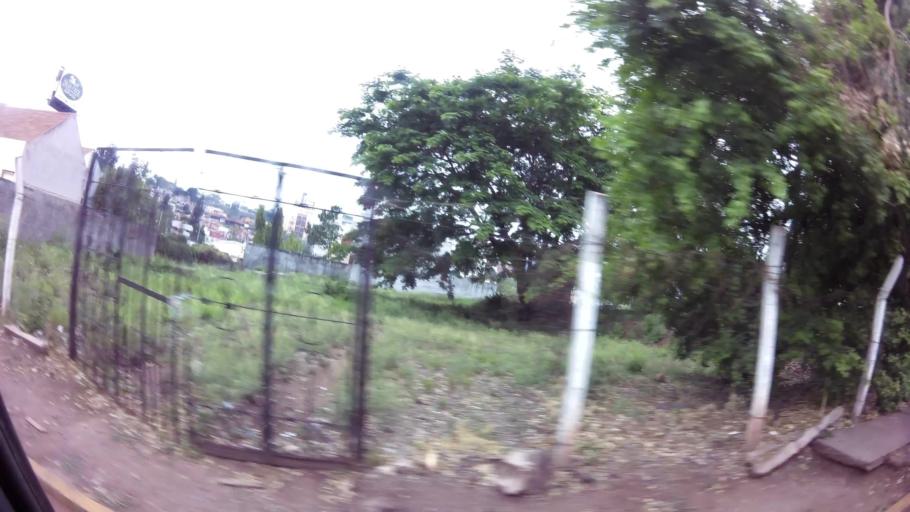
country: HN
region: Francisco Morazan
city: Tegucigalpa
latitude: 14.0893
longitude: -87.1795
